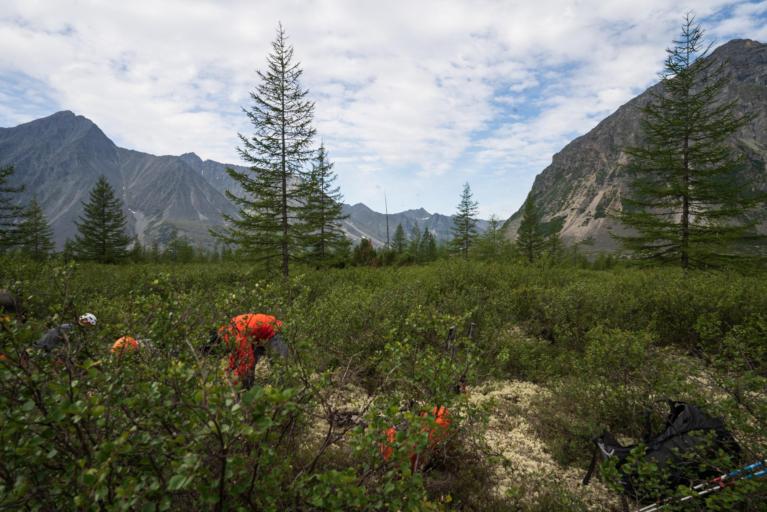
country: RU
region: Transbaikal Territory
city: Chara
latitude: 56.8667
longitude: 117.3021
